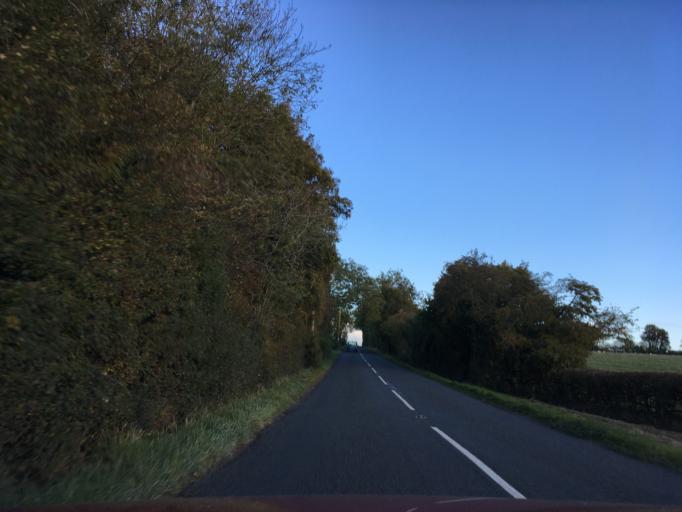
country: GB
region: England
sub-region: Worcestershire
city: Upton upon Severn
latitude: 52.0126
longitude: -2.2975
